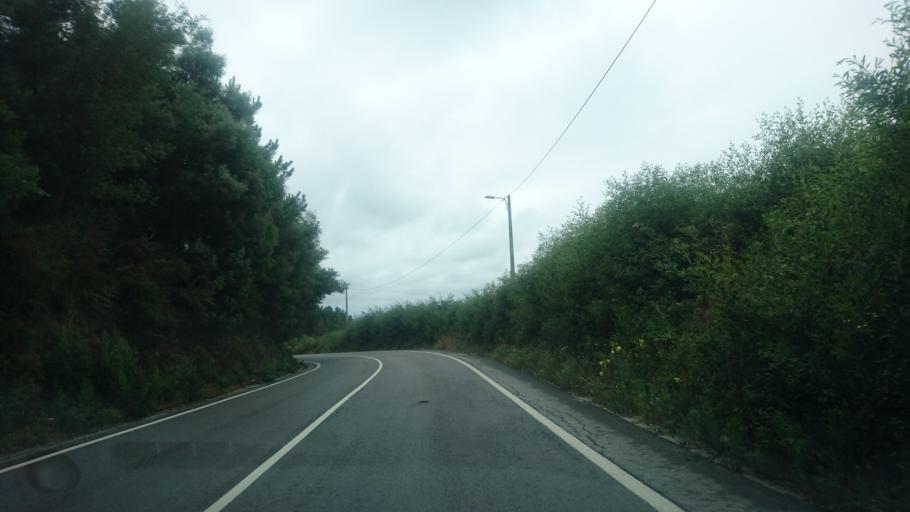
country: PT
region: Aveiro
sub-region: Santa Maria da Feira
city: Sao Joao de Ver
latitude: 40.9608
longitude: -8.5456
